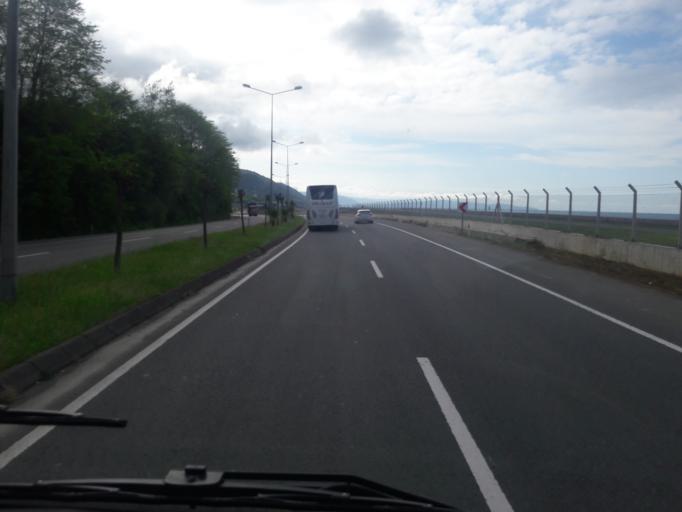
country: TR
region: Giresun
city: Piraziz
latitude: 40.9624
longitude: 38.0974
